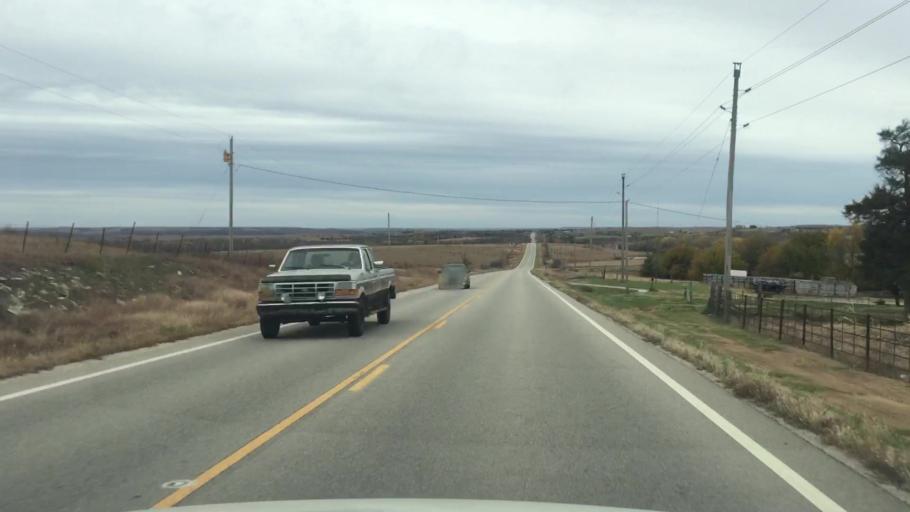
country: US
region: Kansas
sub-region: Wabaunsee County
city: Alma
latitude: 39.0958
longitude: -96.2892
